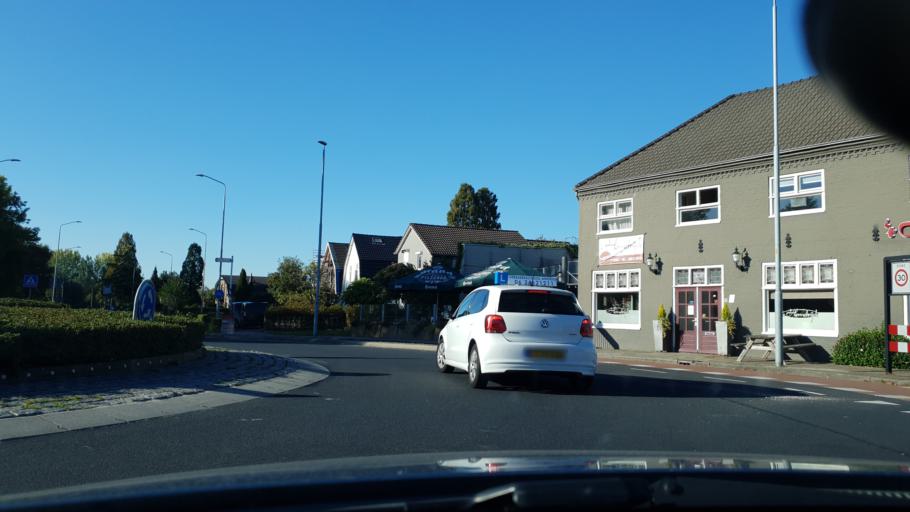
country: NL
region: Gelderland
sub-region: Gemeente Beuningen
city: Beuningen
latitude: 51.8652
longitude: 5.7719
